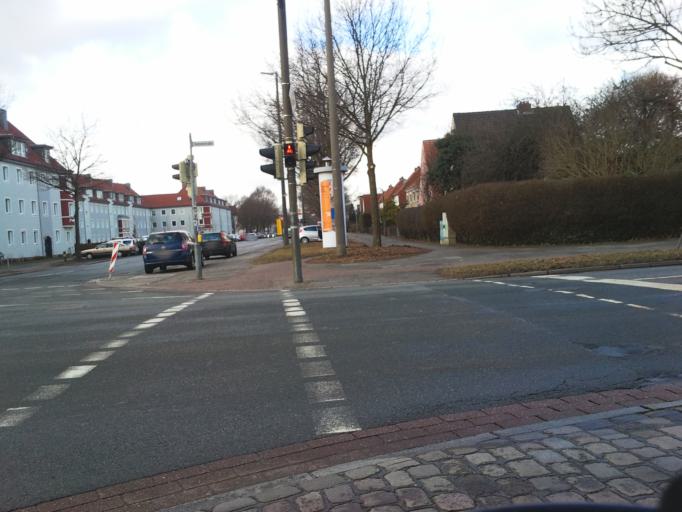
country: DE
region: Bremen
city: Bremen
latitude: 53.0983
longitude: 8.8128
